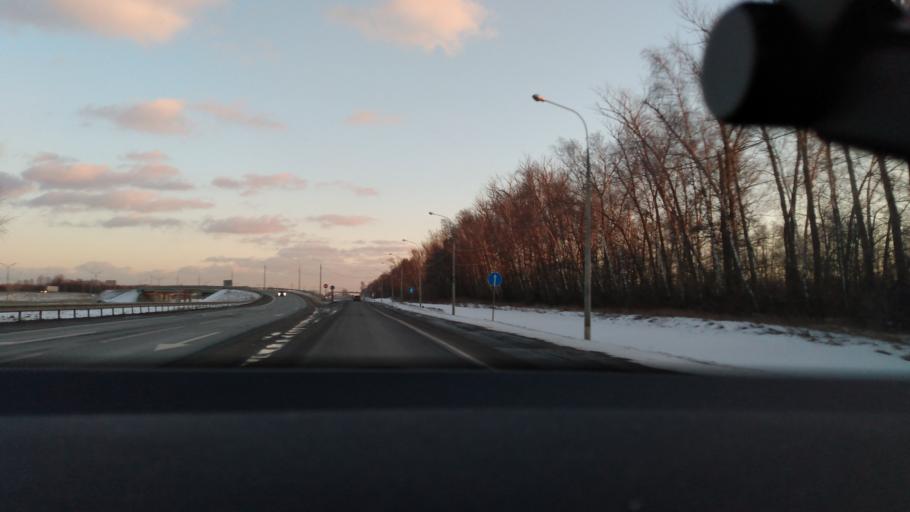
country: RU
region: Moskovskaya
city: Raduzhnyy
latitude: 55.1672
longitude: 38.6707
